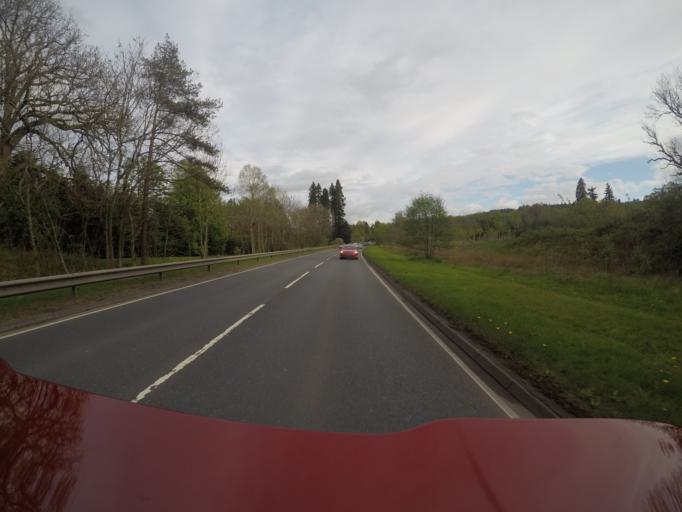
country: GB
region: Scotland
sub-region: West Dunbartonshire
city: Balloch
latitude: 56.0175
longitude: -4.6149
